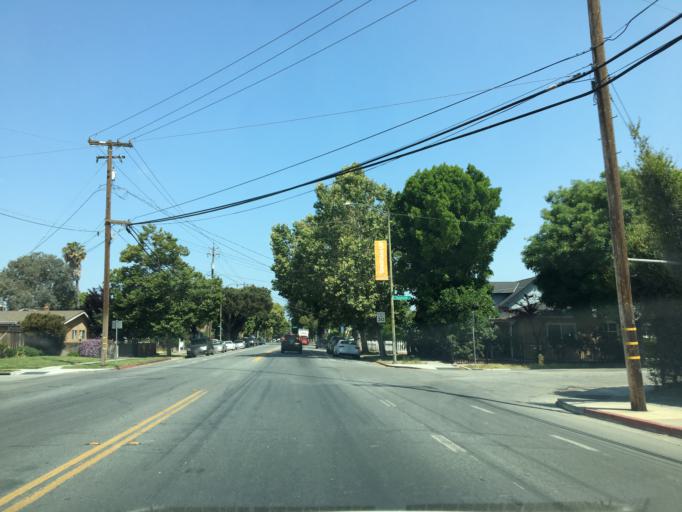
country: US
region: California
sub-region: Santa Clara County
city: San Jose
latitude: 37.3211
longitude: -121.8707
